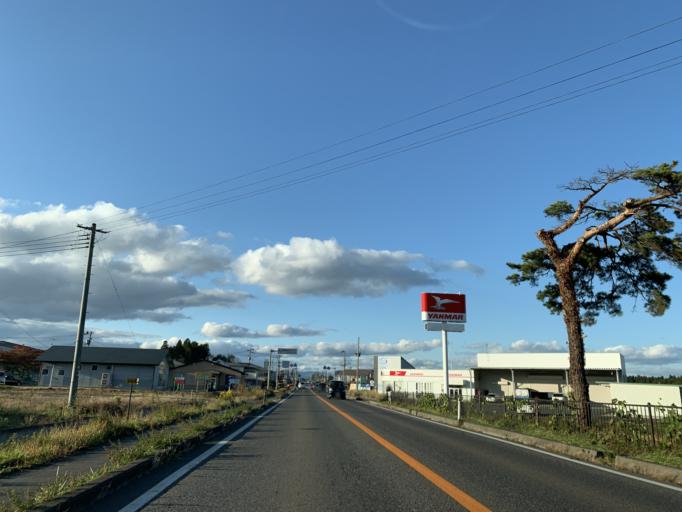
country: JP
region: Iwate
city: Kitakami
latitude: 39.2131
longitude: 141.1040
